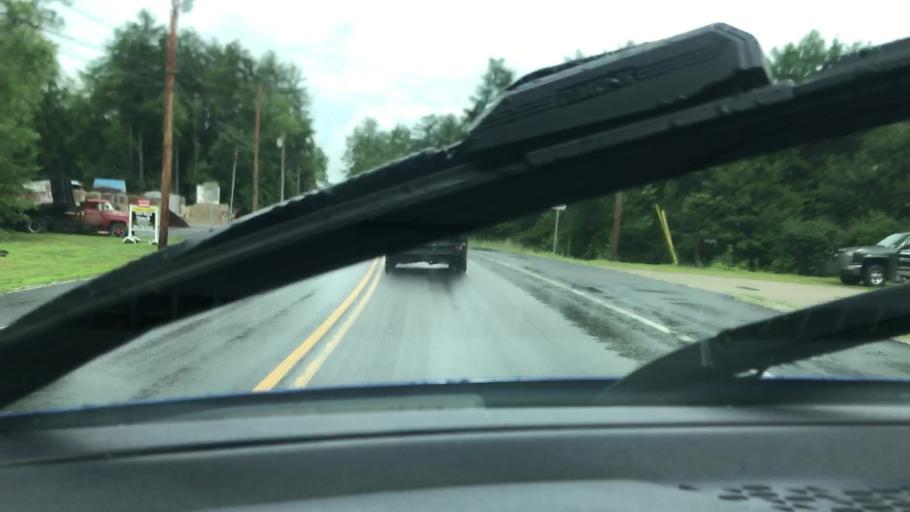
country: US
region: New Hampshire
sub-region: Merrimack County
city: Epsom
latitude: 43.2218
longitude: -71.3268
